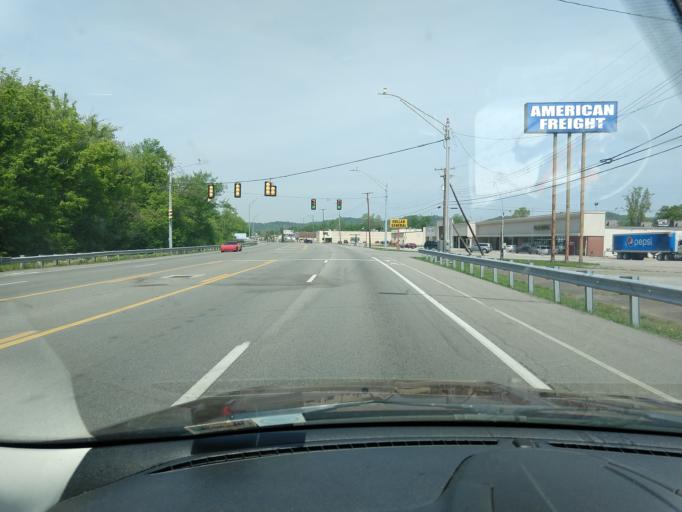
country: US
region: West Virginia
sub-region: Kanawha County
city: Dunbar
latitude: 38.3681
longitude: -81.7657
